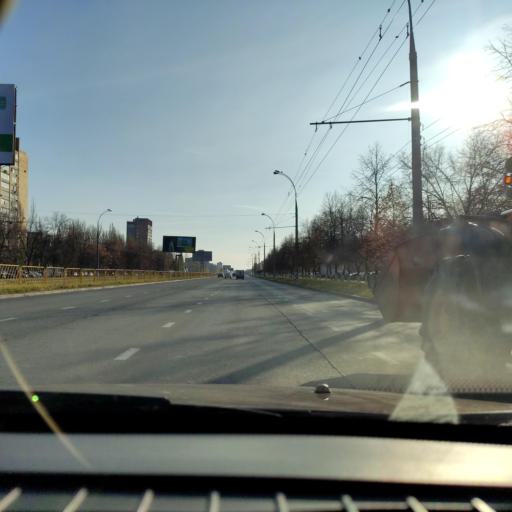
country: RU
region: Samara
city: Tol'yatti
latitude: 53.5247
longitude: 49.2962
